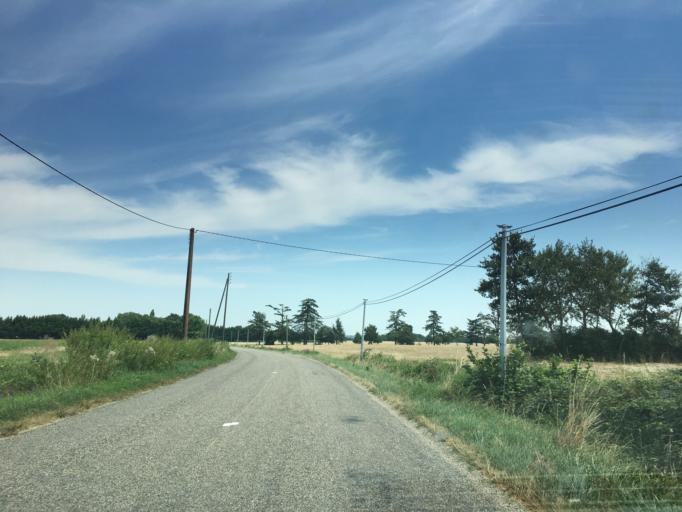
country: FR
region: Midi-Pyrenees
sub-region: Departement du Gers
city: Fleurance
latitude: 43.8157
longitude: 0.6229
